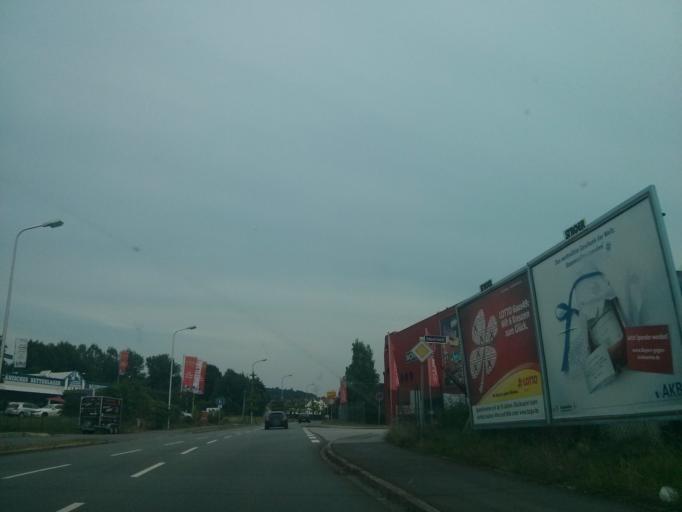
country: DE
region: Bavaria
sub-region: Lower Bavaria
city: Deggendorf
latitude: 48.8529
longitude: 12.9626
